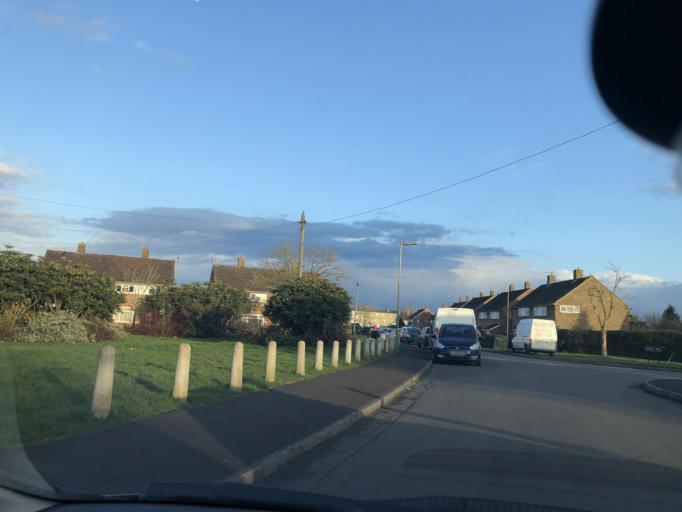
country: GB
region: England
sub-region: Oxfordshire
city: Witney
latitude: 51.7887
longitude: -1.5052
